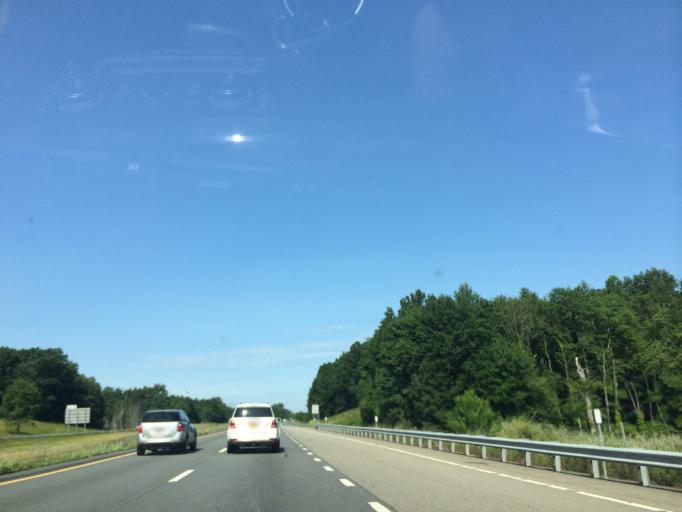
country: US
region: New York
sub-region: Orange County
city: Orange Lake
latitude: 41.5123
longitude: -74.1373
